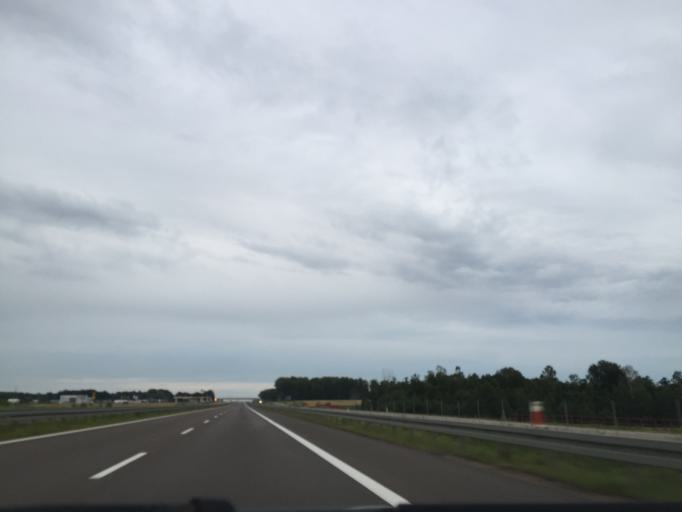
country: PL
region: Podlasie
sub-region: Powiat bialostocki
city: Tykocin
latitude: 53.1413
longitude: 22.7813
